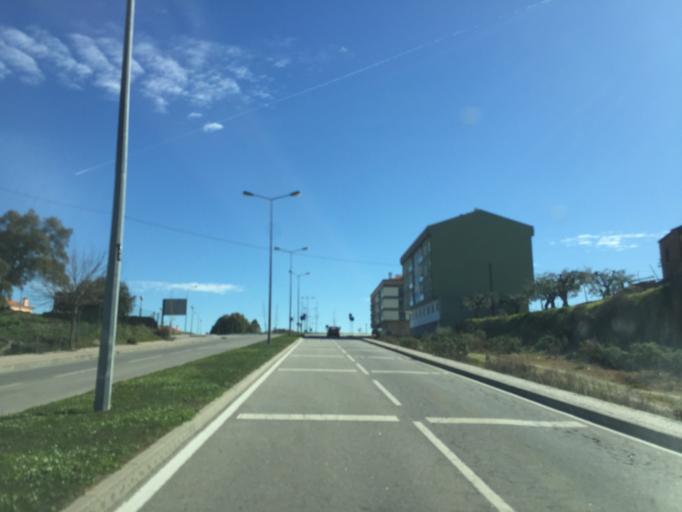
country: PT
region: Castelo Branco
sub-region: Castelo Branco
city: Castelo Branco
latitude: 39.8341
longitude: -7.4903
